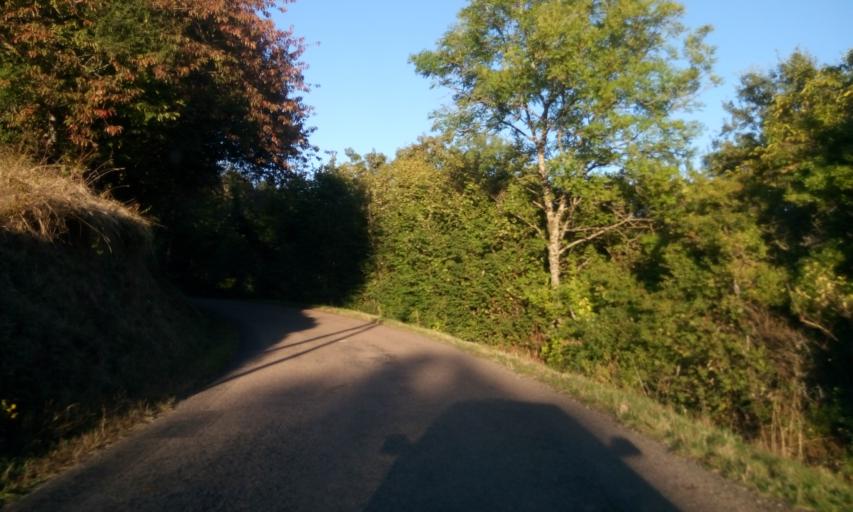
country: FR
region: Rhone-Alpes
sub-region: Departement du Rhone
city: Grandris
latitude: 45.9682
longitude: 4.4677
